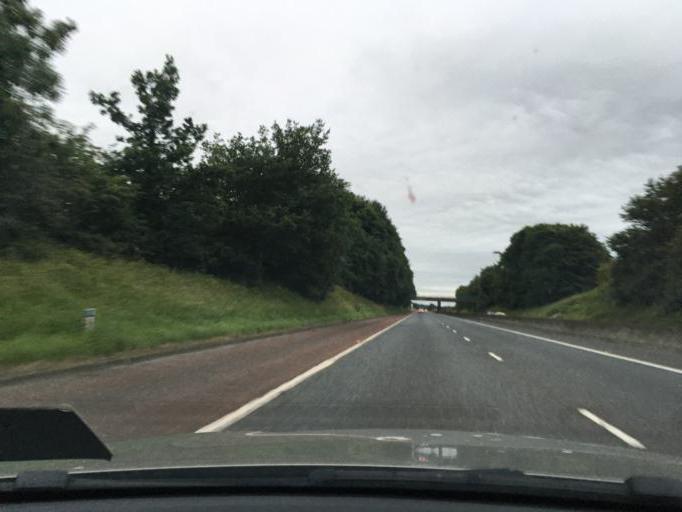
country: GB
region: Northern Ireland
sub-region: Lisburn District
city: Lisburn
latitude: 54.5354
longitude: -5.9971
